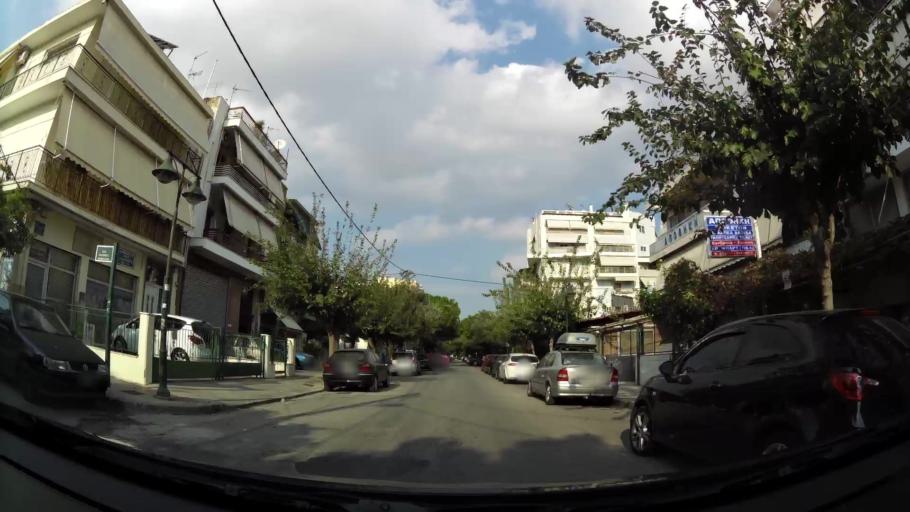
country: GR
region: Attica
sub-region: Nomarchia Athinas
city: Moskhaton
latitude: 37.9441
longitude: 23.6886
